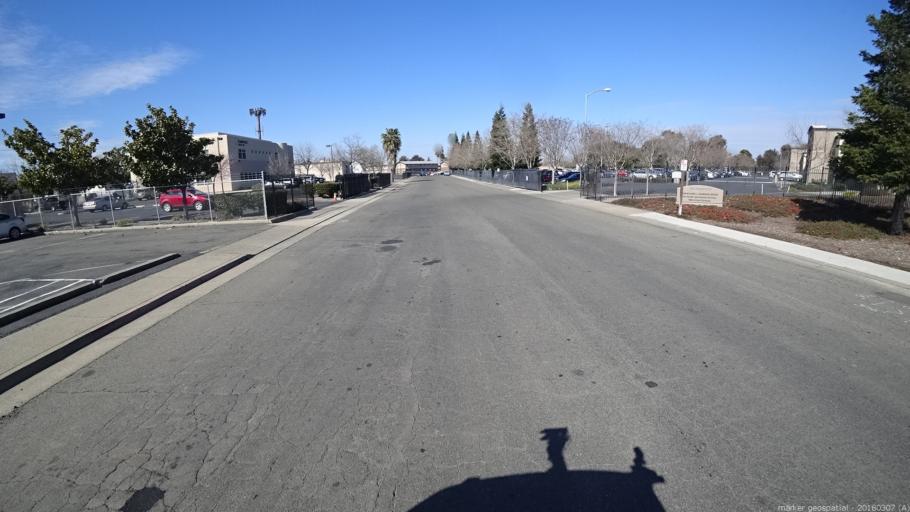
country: US
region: California
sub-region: Sacramento County
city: Parkway
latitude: 38.4975
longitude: -121.4508
